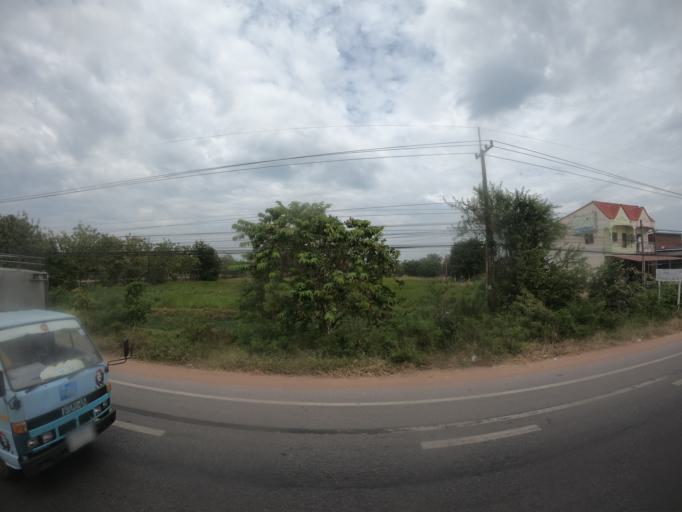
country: TH
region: Maha Sarakham
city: Maha Sarakham
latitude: 16.1639
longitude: 103.3400
